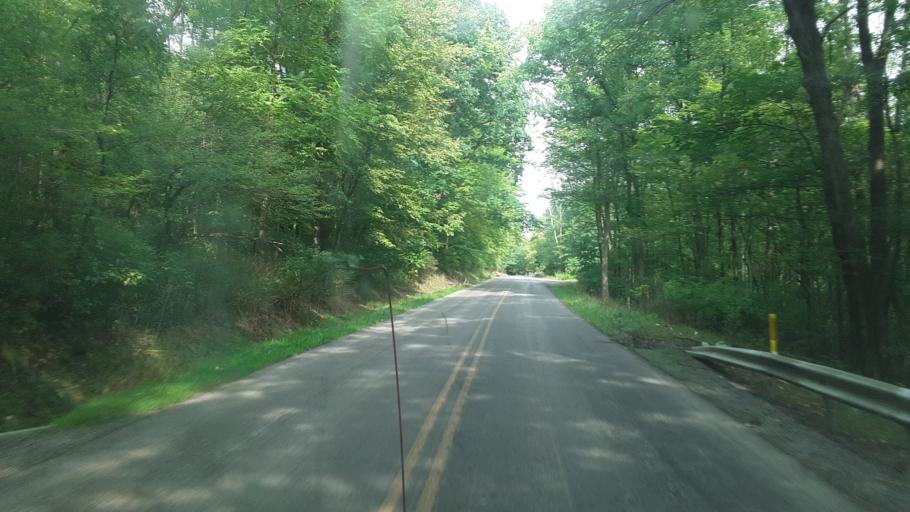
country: US
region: Pennsylvania
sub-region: Jefferson County
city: Punxsutawney
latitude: 40.9045
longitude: -79.0414
